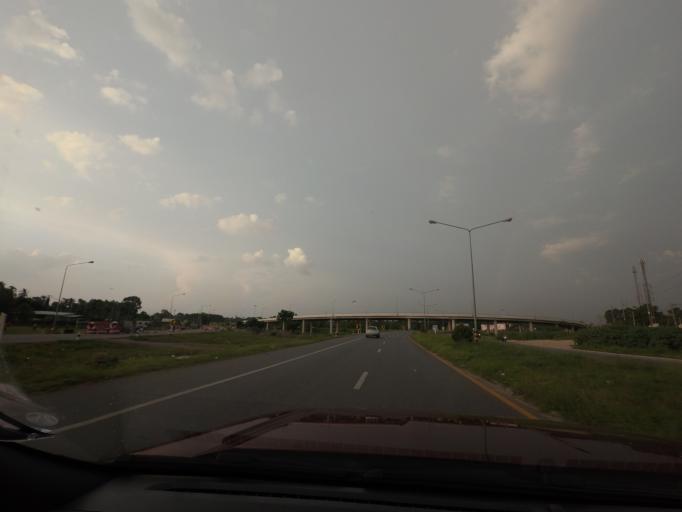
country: TH
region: Yala
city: Yala
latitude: 6.5523
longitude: 101.2599
